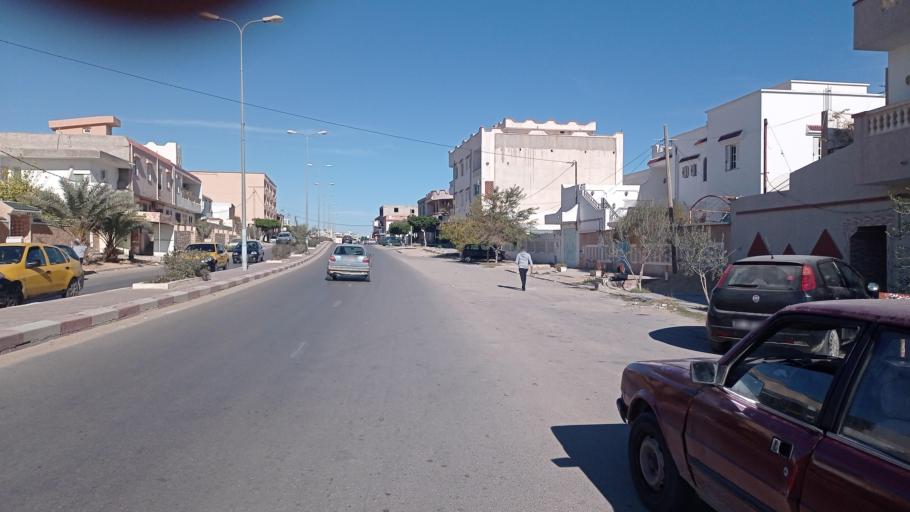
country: TN
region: Qabis
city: Gabes
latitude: 33.8457
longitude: 10.1133
